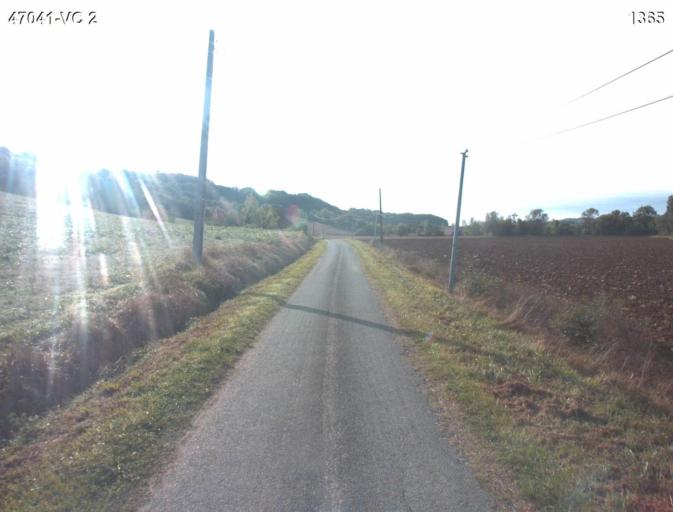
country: FR
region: Aquitaine
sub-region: Departement du Lot-et-Garonne
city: Port-Sainte-Marie
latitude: 44.1909
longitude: 0.4156
